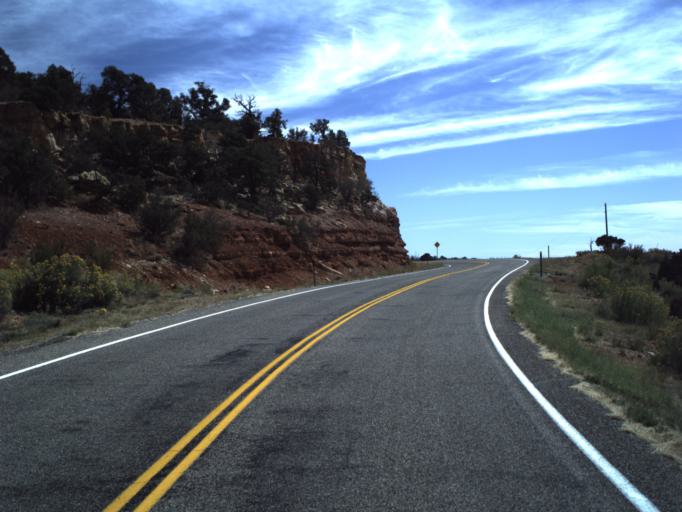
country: US
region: Utah
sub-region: Wayne County
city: Loa
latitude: 37.8939
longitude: -111.4552
